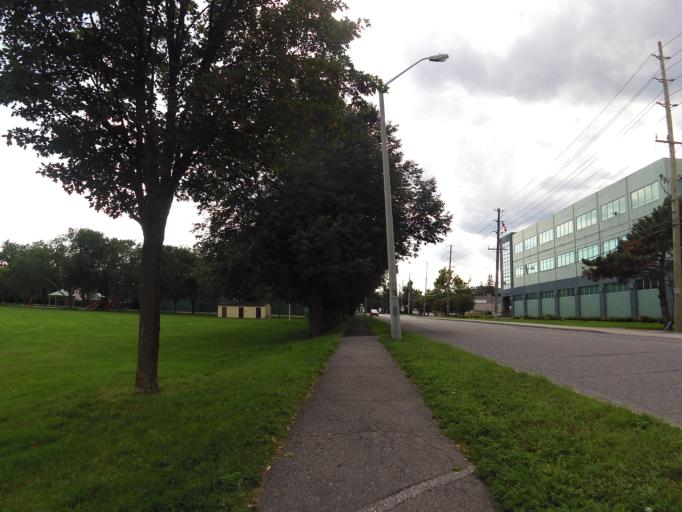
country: CA
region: Ontario
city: Bells Corners
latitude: 45.3456
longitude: -75.7939
